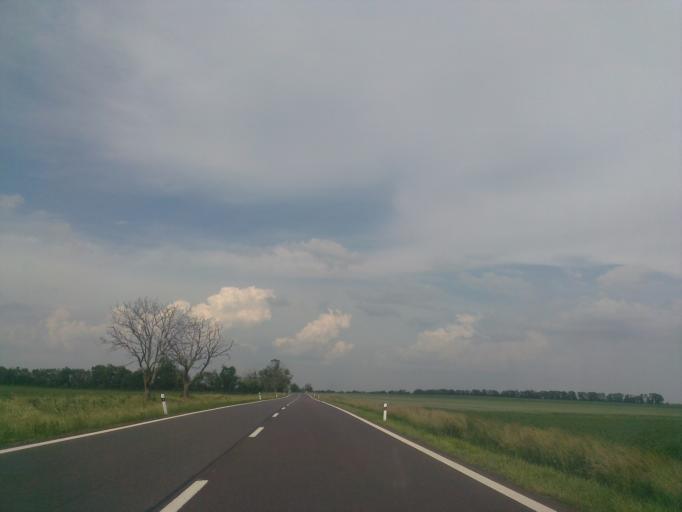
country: CZ
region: South Moravian
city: Miroslav
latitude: 48.9079
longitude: 16.3109
